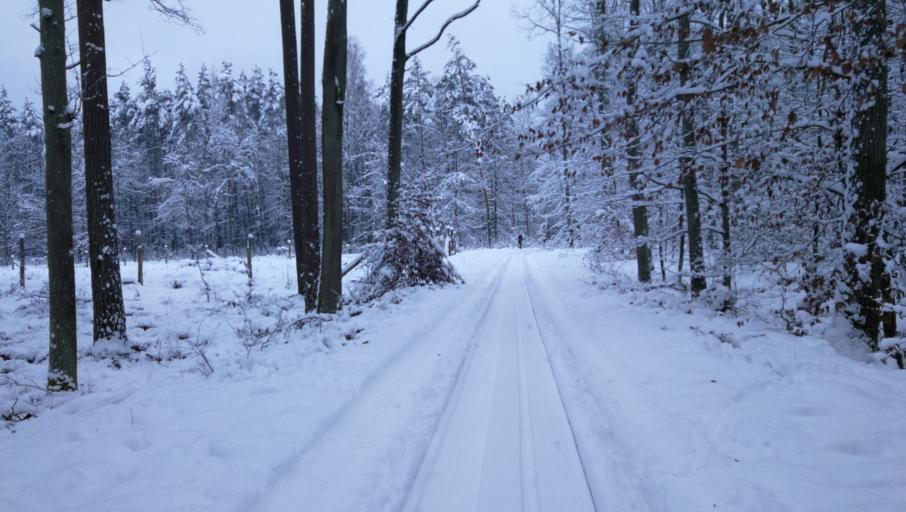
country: PL
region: Kujawsko-Pomorskie
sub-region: Powiat brodnicki
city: Gorzno
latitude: 53.2009
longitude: 19.6991
